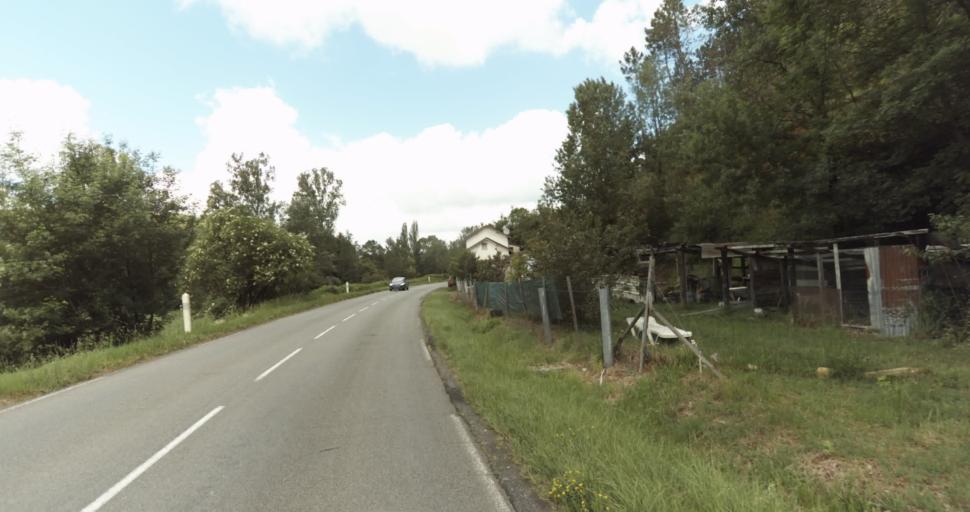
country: FR
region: Aquitaine
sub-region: Departement de la Dordogne
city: Beaumont-du-Perigord
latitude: 44.7880
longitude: 0.7603
